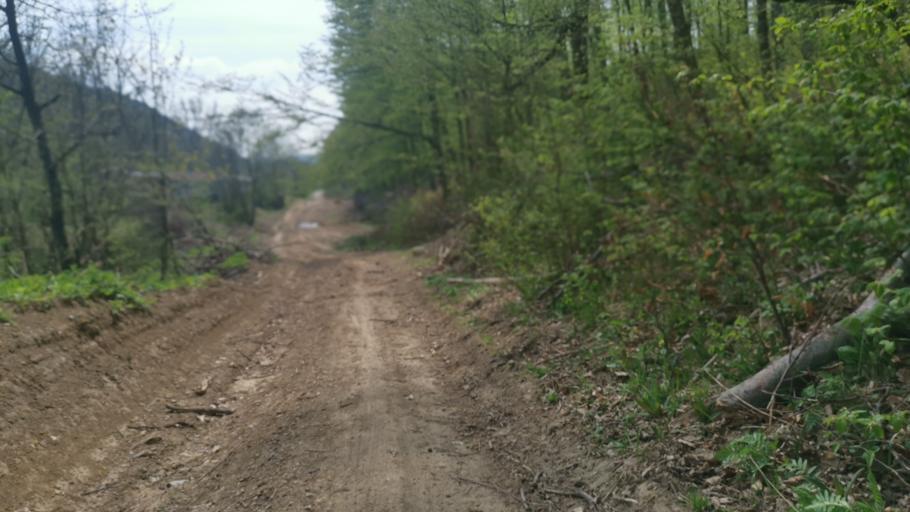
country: SK
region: Trnavsky
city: Smolenice
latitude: 48.5559
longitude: 17.4531
